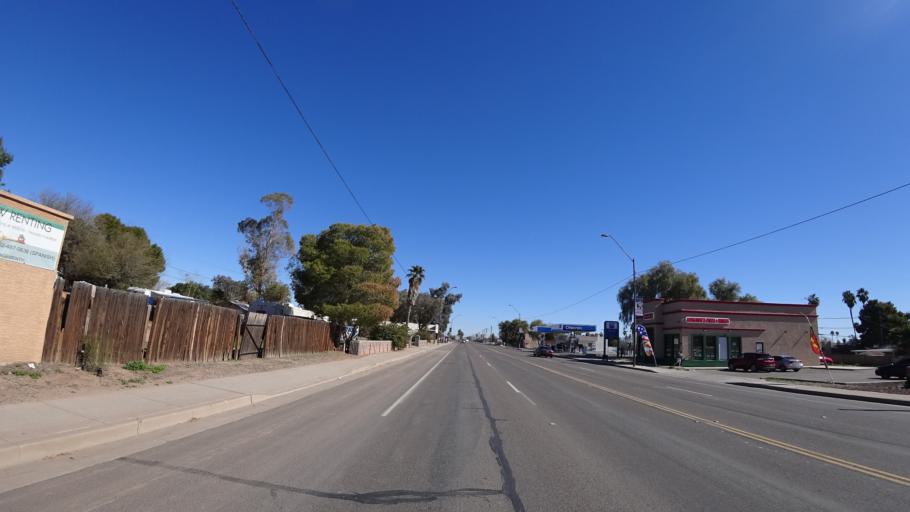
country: US
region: Arizona
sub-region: Maricopa County
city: Buckeye
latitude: 33.3706
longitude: -112.5797
